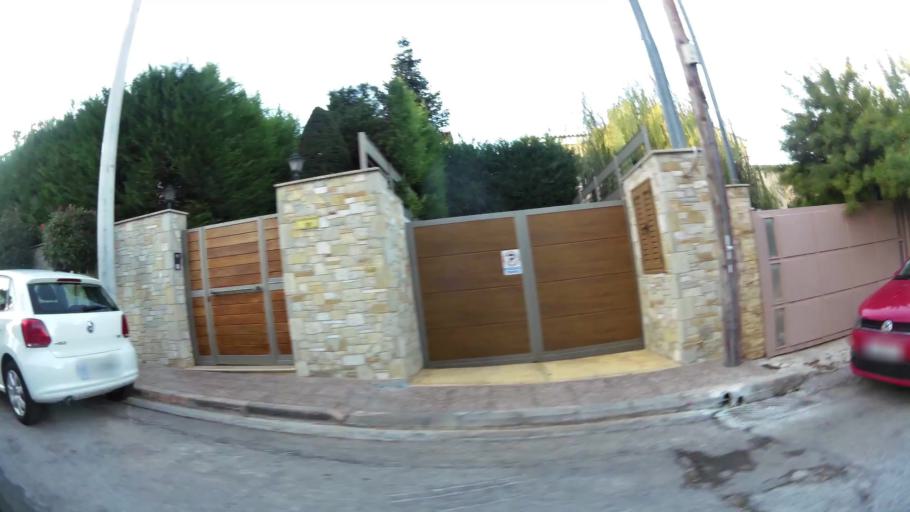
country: GR
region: Attica
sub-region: Nomarchia Anatolikis Attikis
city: Kryoneri
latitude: 38.1440
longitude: 23.8337
